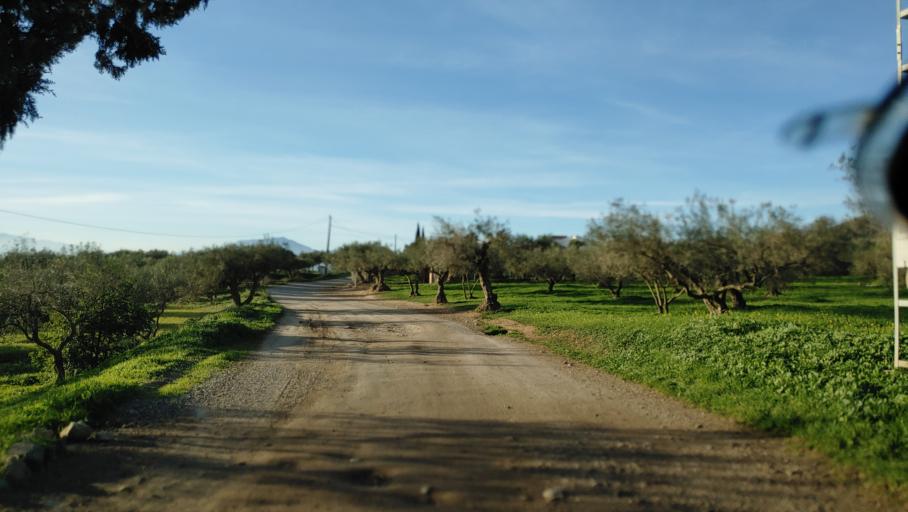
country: ES
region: Andalusia
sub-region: Provincia de Malaga
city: Cartama
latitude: 36.6826
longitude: -4.6427
